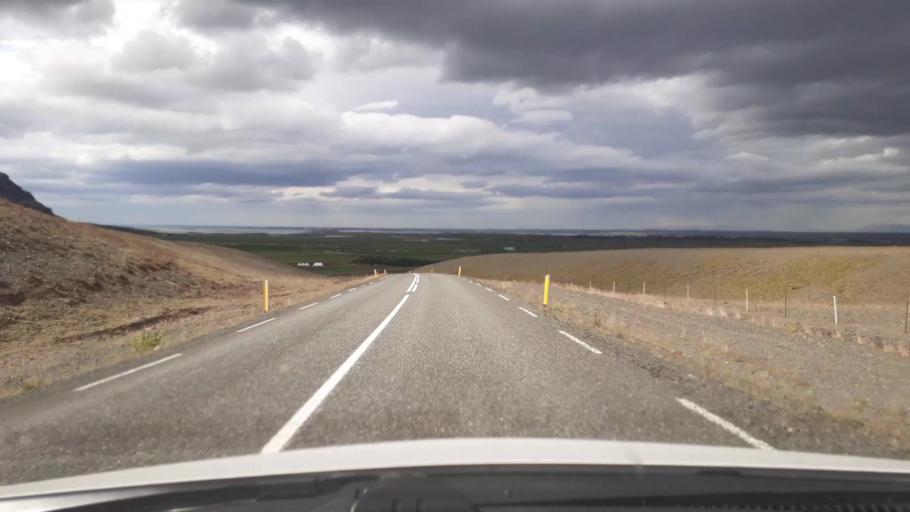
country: IS
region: West
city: Borgarnes
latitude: 64.5455
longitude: -21.6763
